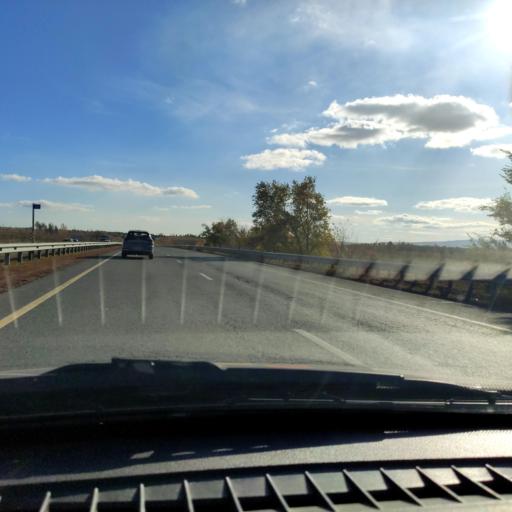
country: RU
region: Samara
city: Zhigulevsk
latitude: 53.5132
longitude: 49.5375
